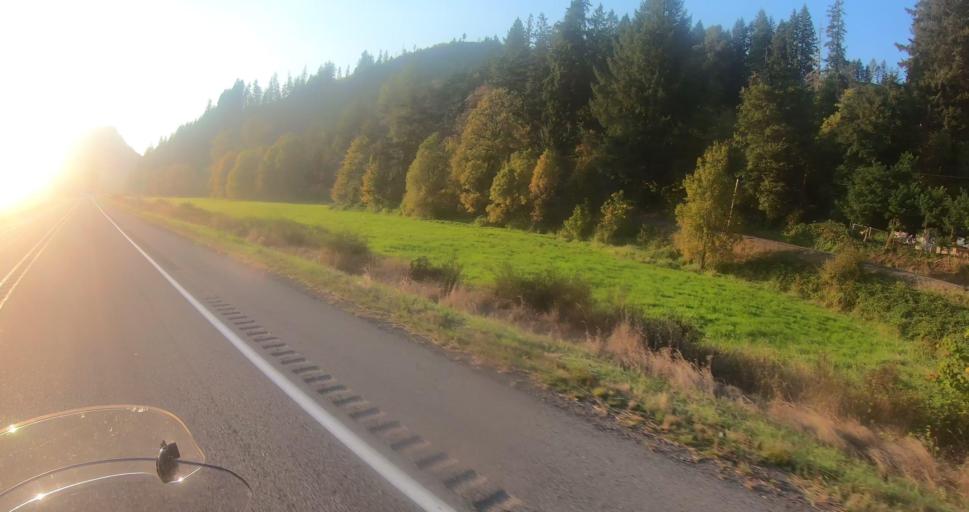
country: US
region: Washington
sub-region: Lewis County
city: Morton
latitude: 46.5356
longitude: -121.9625
